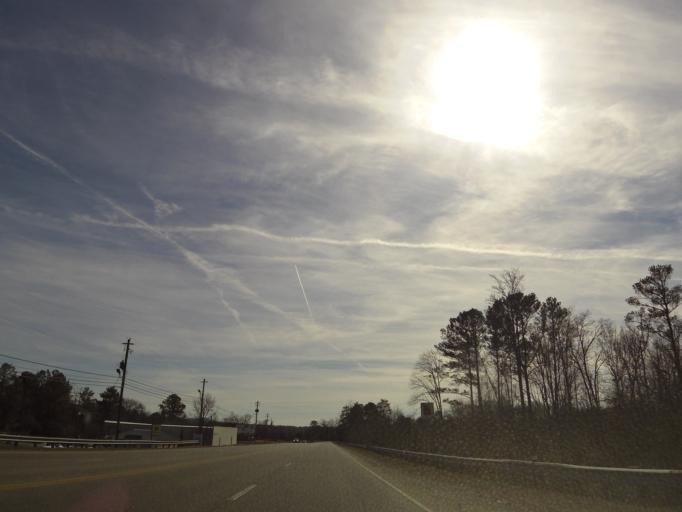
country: US
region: Georgia
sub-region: Murray County
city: Chatsworth
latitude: 34.7418
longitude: -84.7637
